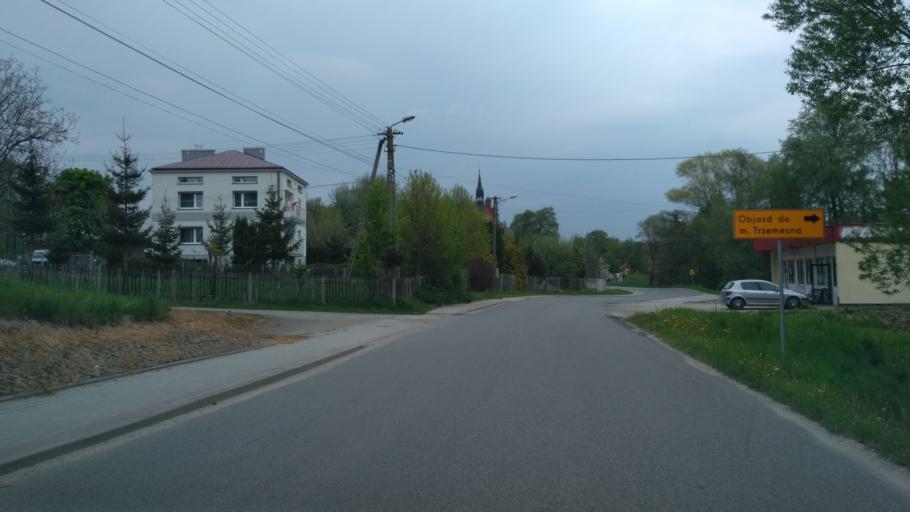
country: PL
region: Lesser Poland Voivodeship
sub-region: Powiat tarnowski
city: Skrzyszow
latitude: 49.9691
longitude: 21.0551
